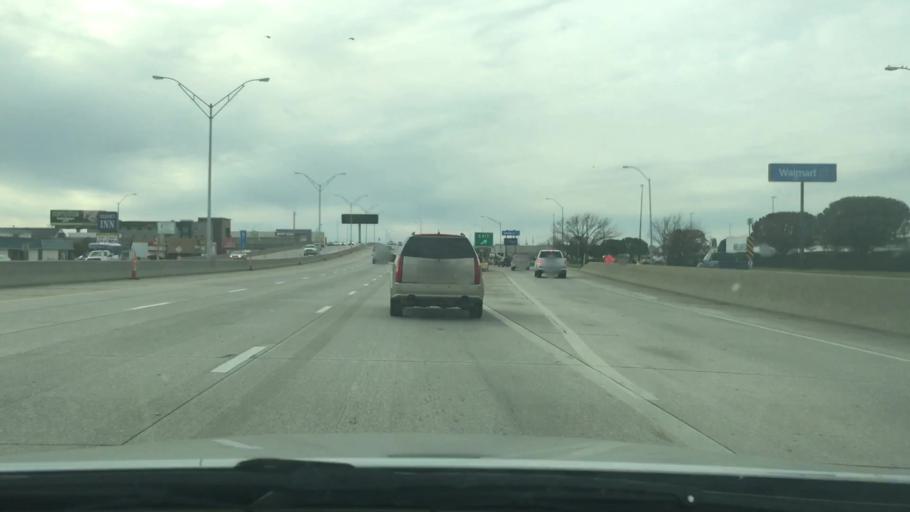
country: US
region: Kansas
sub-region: Sedgwick County
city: Wichita
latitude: 37.6731
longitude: -97.4120
